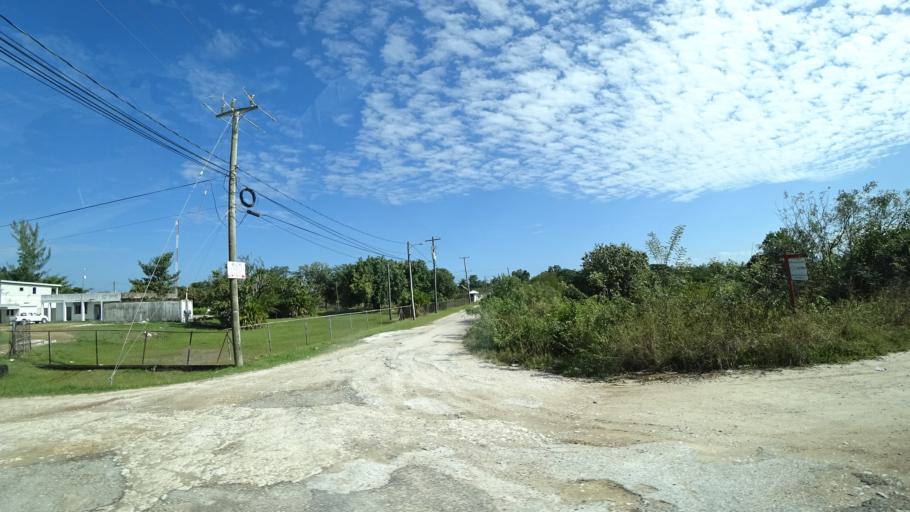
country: BZ
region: Belize
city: Belize City
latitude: 17.5635
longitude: -88.3247
